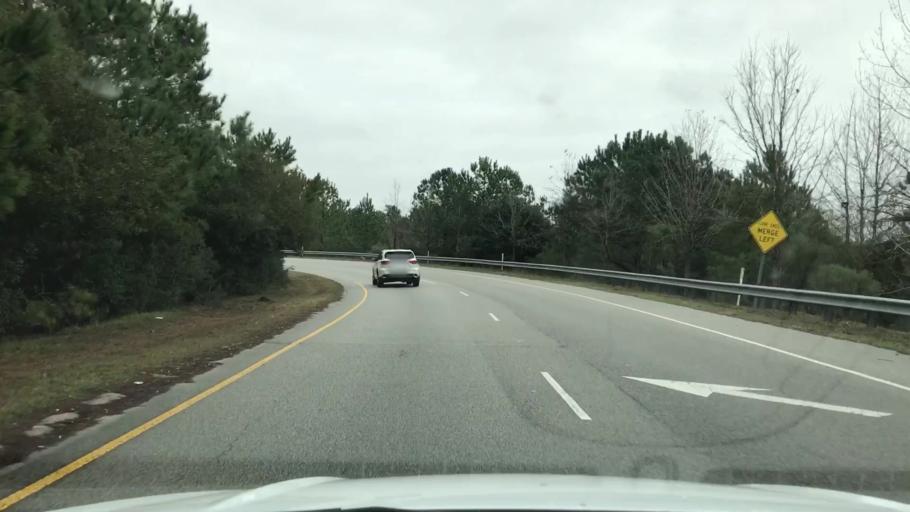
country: US
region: South Carolina
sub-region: Horry County
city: Myrtle Beach
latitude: 33.7378
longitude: -78.8492
